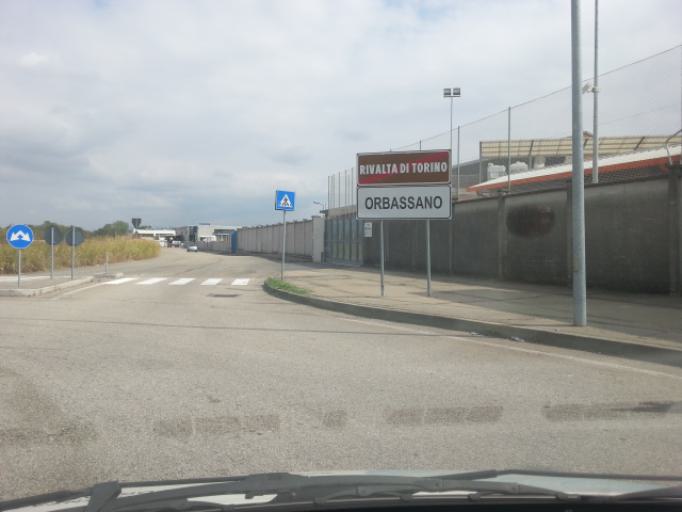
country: IT
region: Piedmont
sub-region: Provincia di Torino
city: Pasta
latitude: 45.0138
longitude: 7.5572
